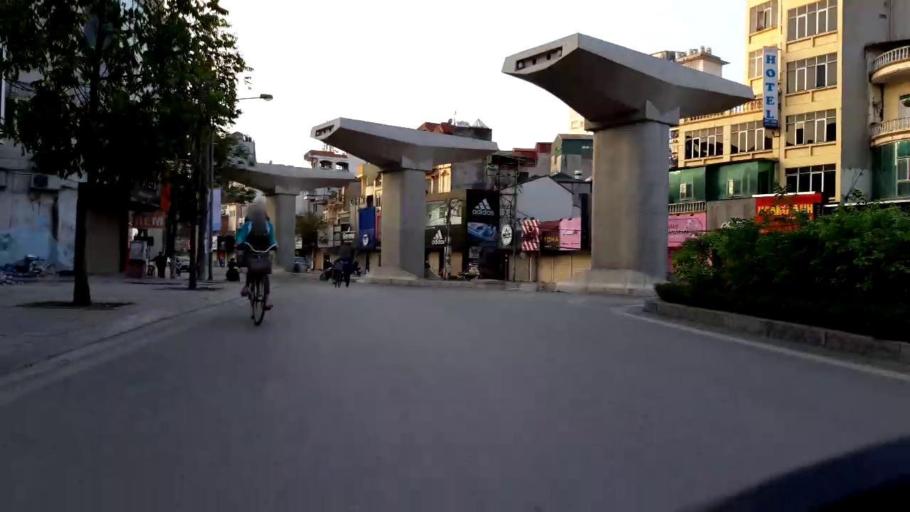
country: VN
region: Ha Noi
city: Cau Giay
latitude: 21.0339
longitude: 105.7977
